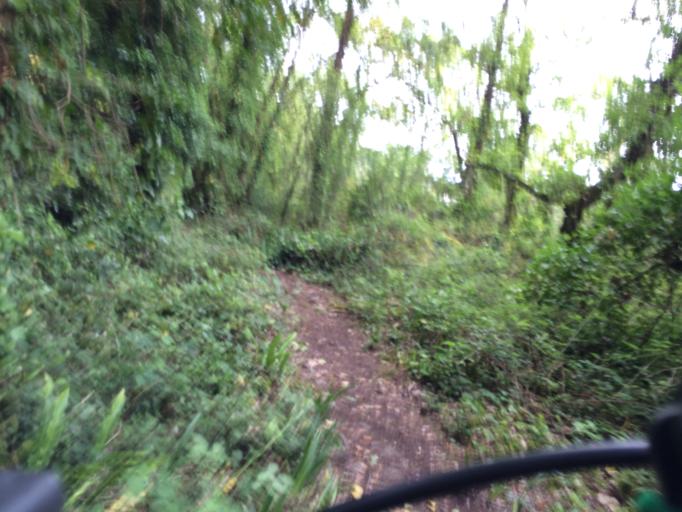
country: FR
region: Brittany
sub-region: Departement du Finistere
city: Hopital-Camfrout
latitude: 48.3268
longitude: -4.2543
